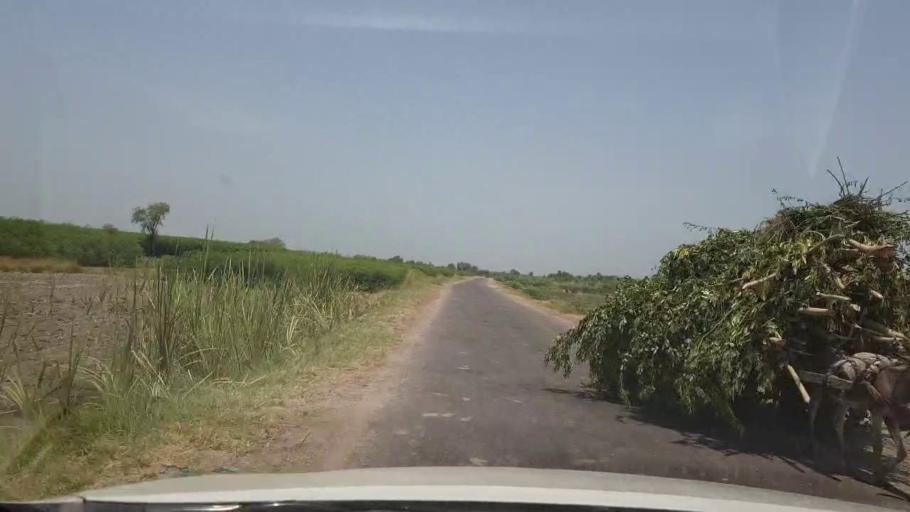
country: PK
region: Sindh
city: Bozdar
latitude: 27.2538
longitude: 68.6396
